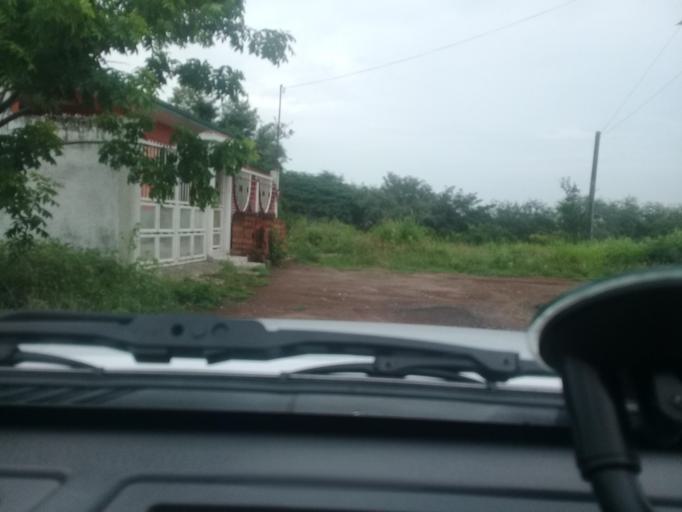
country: MX
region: Veracruz
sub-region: Puente Nacional
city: Cabezas
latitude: 19.3766
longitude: -96.3817
